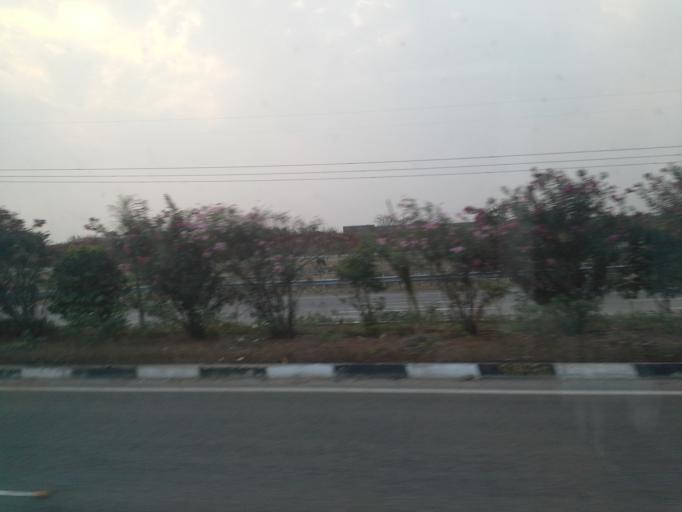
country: IN
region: Telangana
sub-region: Rangareddi
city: Lal Bahadur Nagar
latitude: 17.3103
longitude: 78.6565
